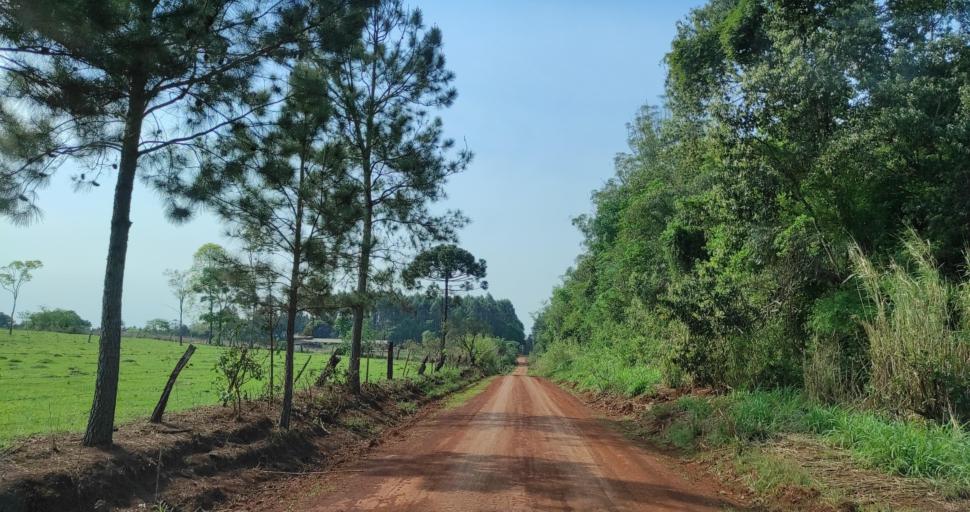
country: AR
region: Misiones
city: Capiovi
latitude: -26.8837
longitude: -55.0483
